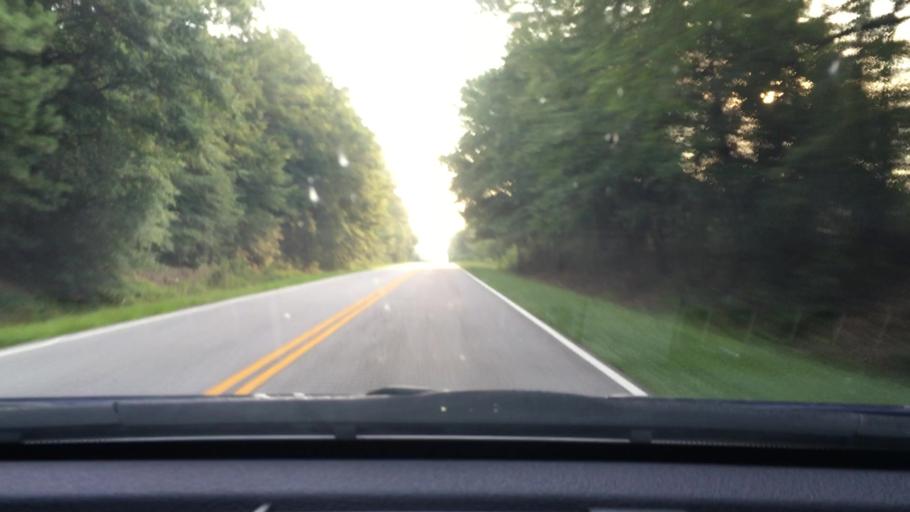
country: US
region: South Carolina
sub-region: Sumter County
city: East Sumter
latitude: 34.0395
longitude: -80.2630
